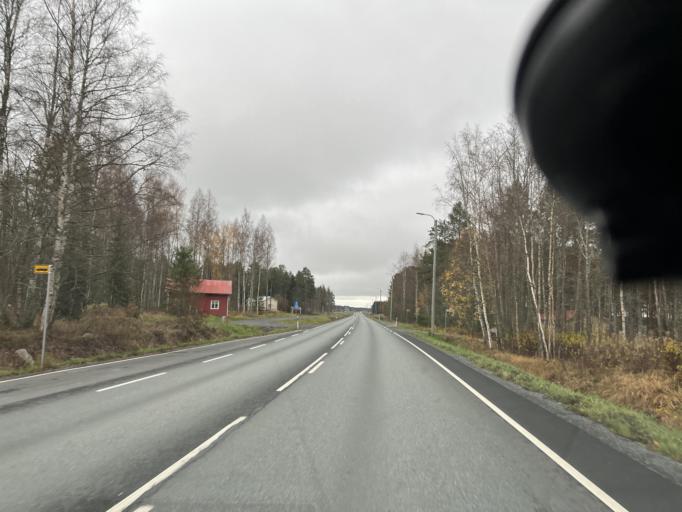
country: FI
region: Northern Ostrobothnia
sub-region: Ylivieska
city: Sievi
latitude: 63.9642
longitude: 24.5003
